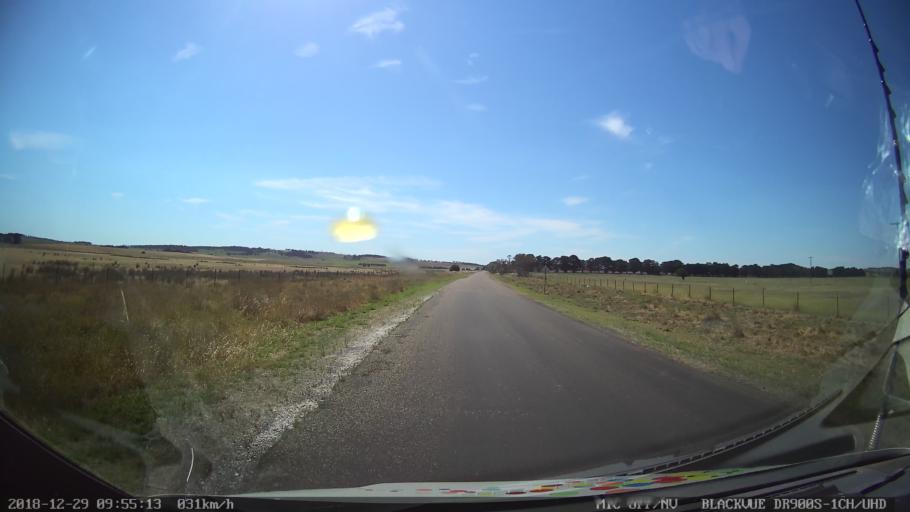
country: AU
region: New South Wales
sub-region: Goulburn Mulwaree
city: Goulburn
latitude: -34.7706
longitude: 149.4673
